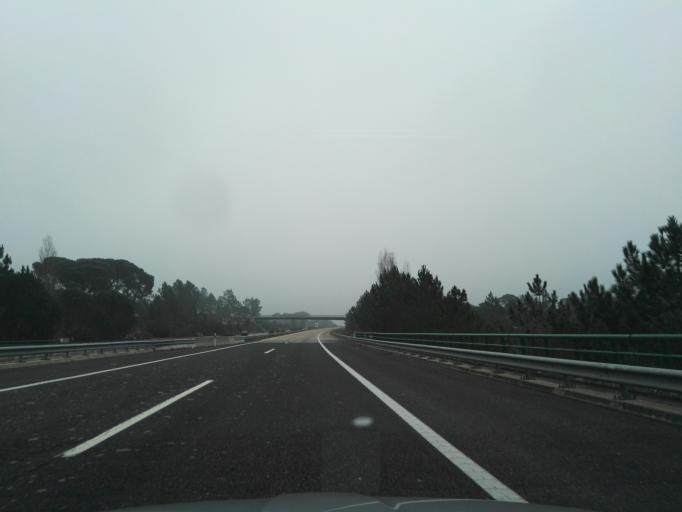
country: PT
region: Evora
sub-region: Vendas Novas
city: Vendas Novas
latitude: 38.6388
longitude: -8.4956
